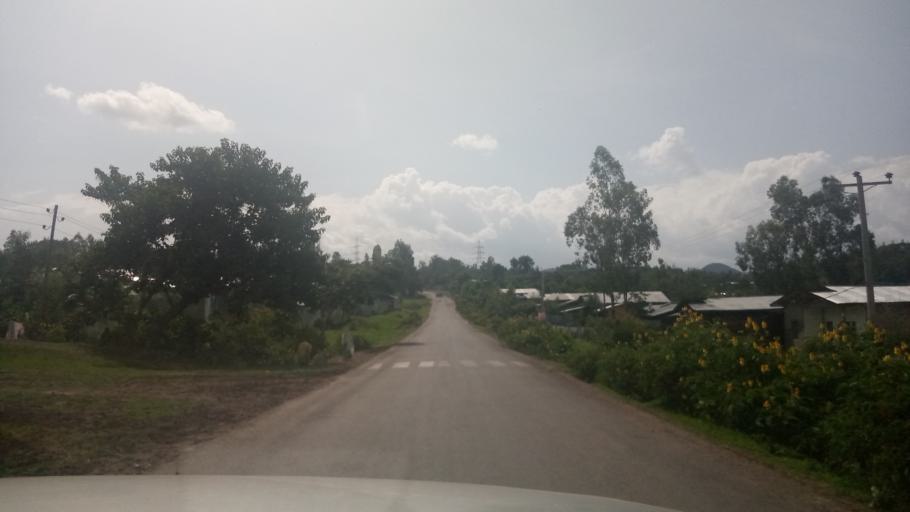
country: ET
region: Oromiya
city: Agaro
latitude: 7.9984
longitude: 36.4994
